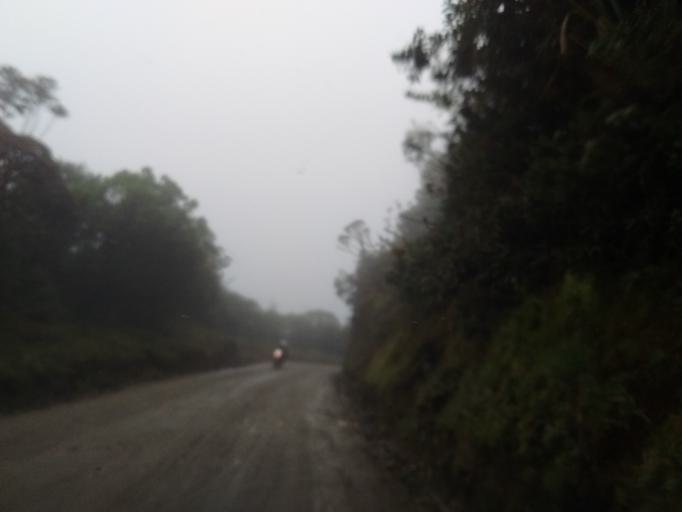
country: CO
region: Cauca
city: Paispamba
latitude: 2.1486
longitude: -76.4459
